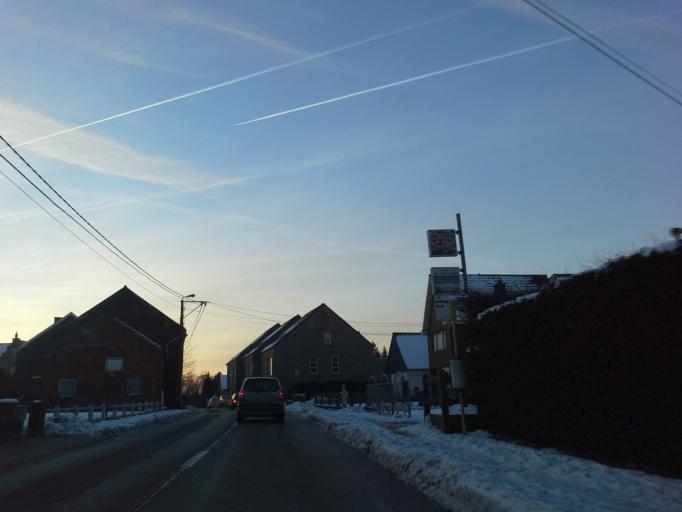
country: BE
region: Flanders
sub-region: Provincie Vlaams-Brabant
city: Lubbeek
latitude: 50.8730
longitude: 4.7944
